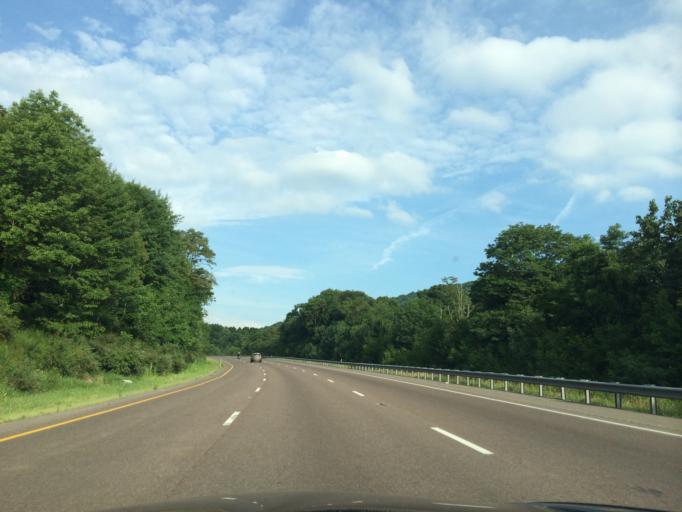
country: US
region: Maryland
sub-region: Allegany County
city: Cresaptown
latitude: 39.6415
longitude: -78.8697
